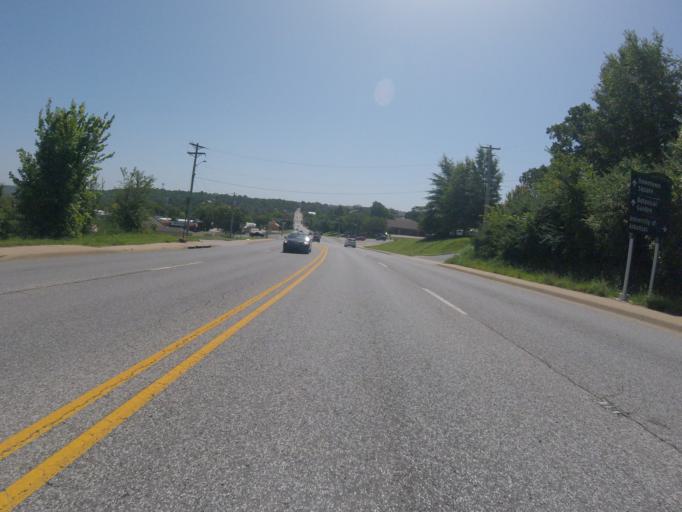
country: US
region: Arkansas
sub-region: Washington County
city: Fayetteville
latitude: 36.0776
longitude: -94.1768
